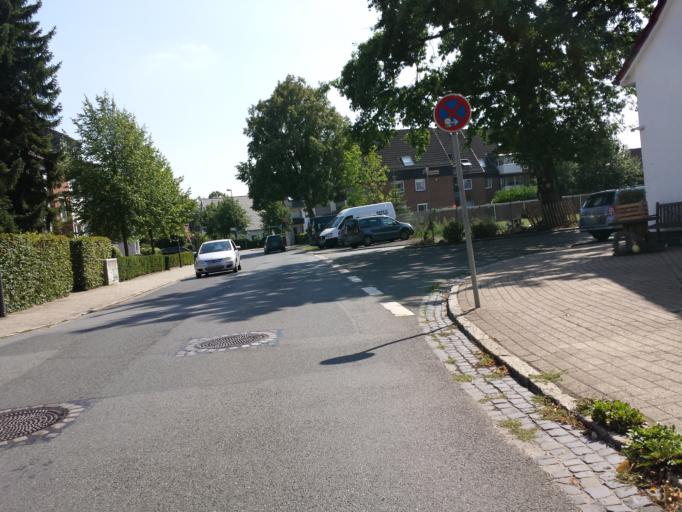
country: DE
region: Bremen
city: Bremen
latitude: 53.0496
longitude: 8.8577
